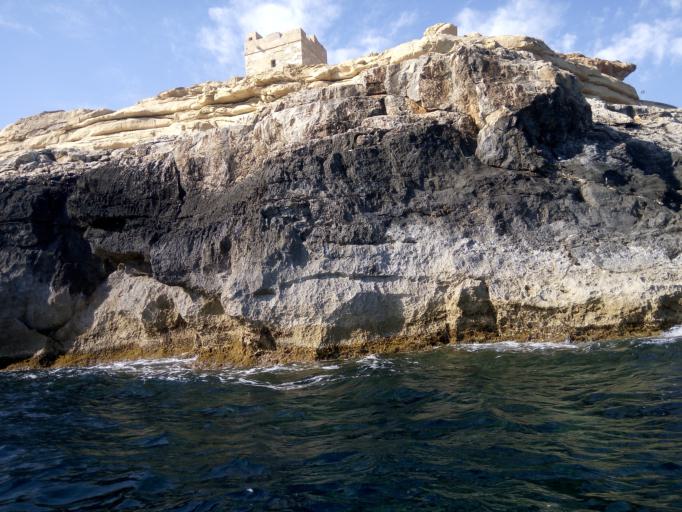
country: MT
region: Il-Qrendi
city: Qrendi
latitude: 35.8189
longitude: 14.4538
